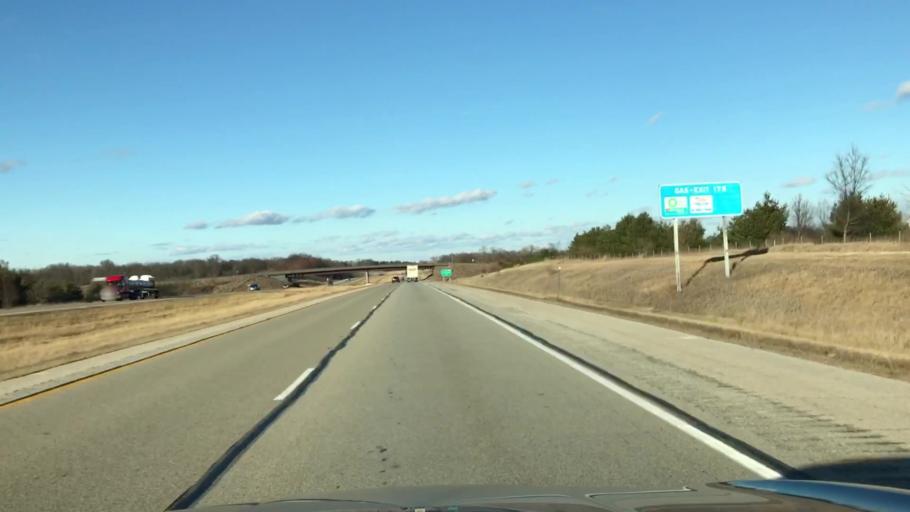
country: US
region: Illinois
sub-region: McLean County
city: Lexington
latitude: 40.6223
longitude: -88.8183
